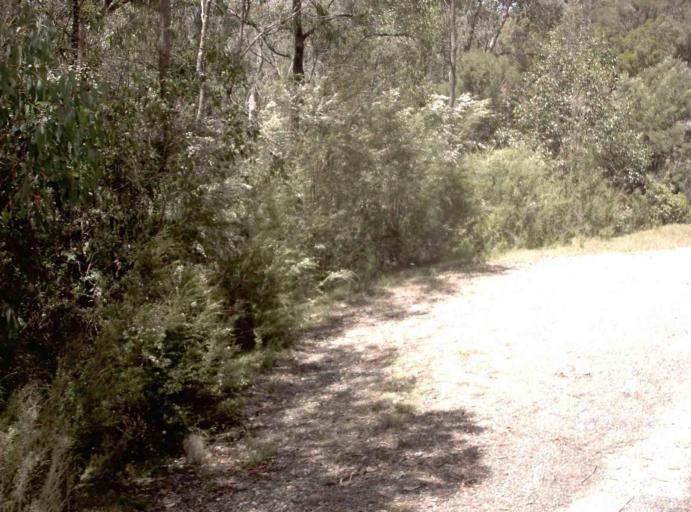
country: AU
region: Victoria
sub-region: East Gippsland
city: Lakes Entrance
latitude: -37.5699
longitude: 147.8900
